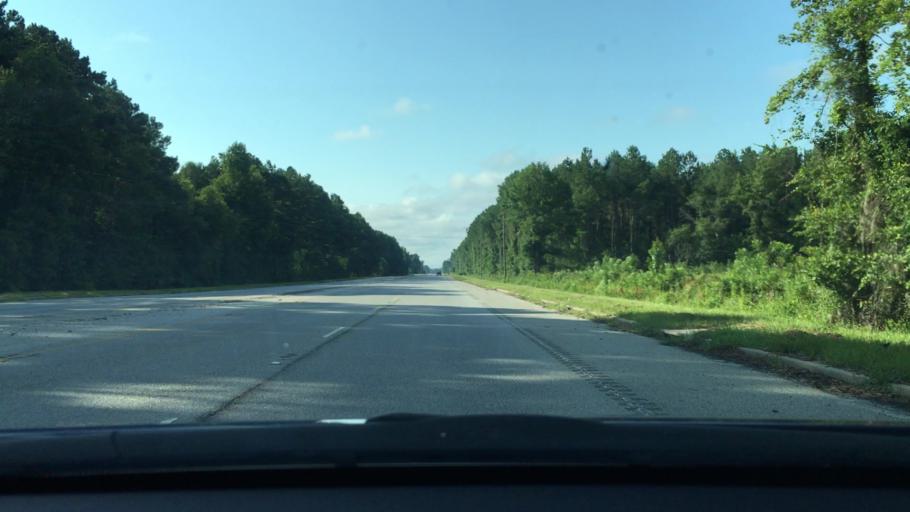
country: US
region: South Carolina
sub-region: Clarendon County
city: Manning
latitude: 33.7741
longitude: -80.2392
